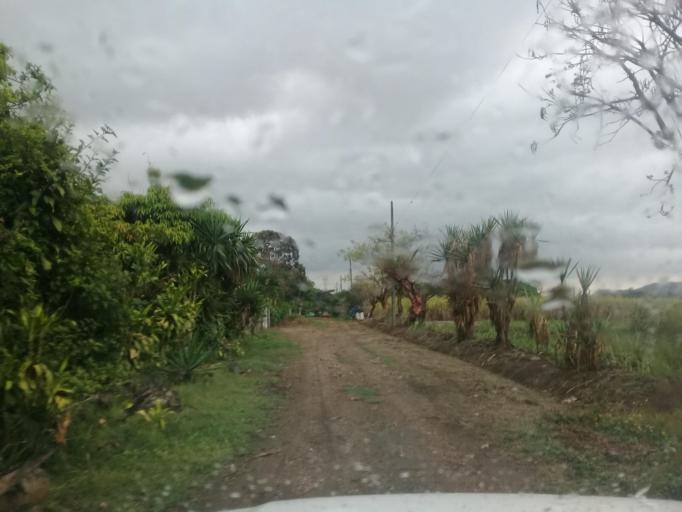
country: MX
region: Veracruz
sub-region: Amatlan de los Reyes
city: Trapiche Viejo
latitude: 18.8419
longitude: -96.9448
